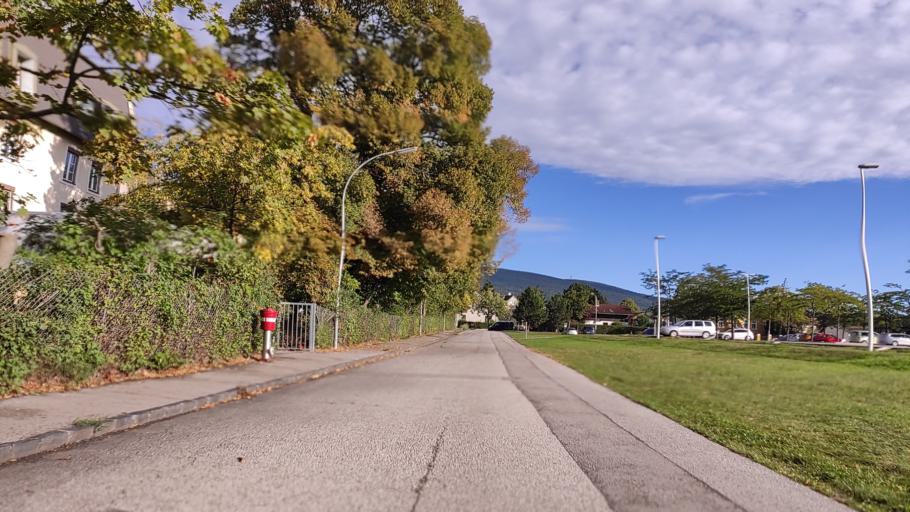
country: AT
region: Lower Austria
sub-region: Politischer Bezirk Baden
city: Pfaffstatten
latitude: 48.0122
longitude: 16.2560
